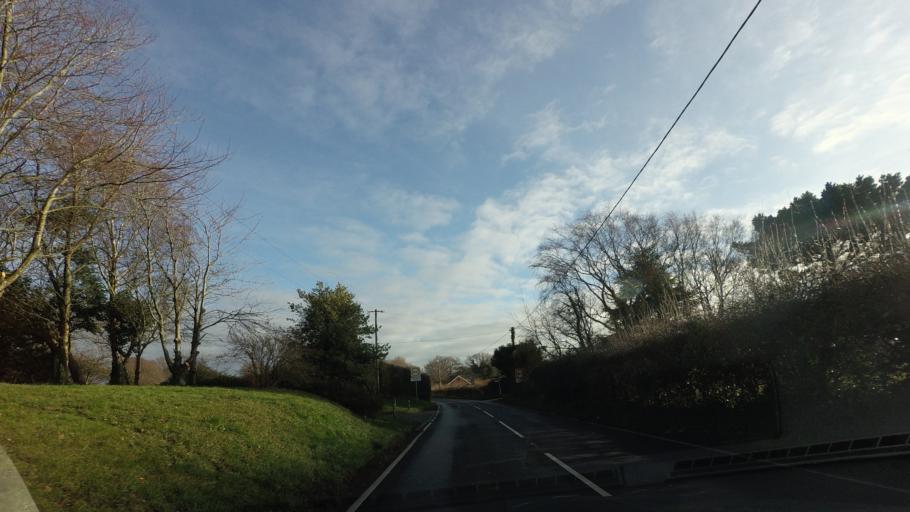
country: GB
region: England
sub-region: East Sussex
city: Bexhill-on-Sea
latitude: 50.8711
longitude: 0.4401
